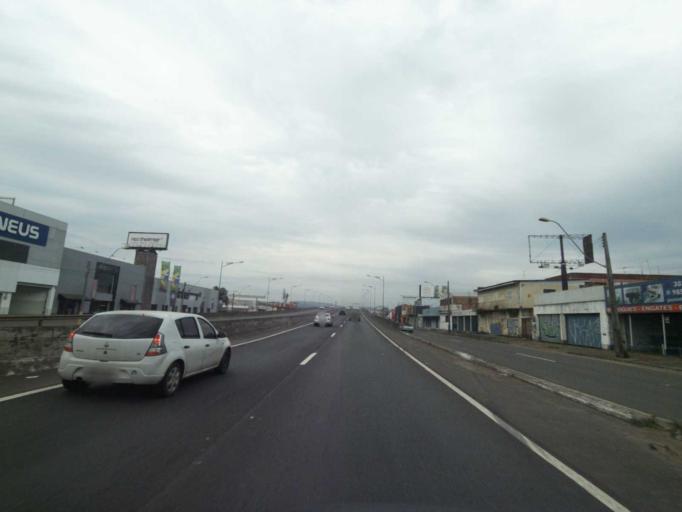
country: BR
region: Rio Grande do Sul
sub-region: Sao Leopoldo
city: Sao Leopoldo
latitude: -29.7700
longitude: -51.1534
